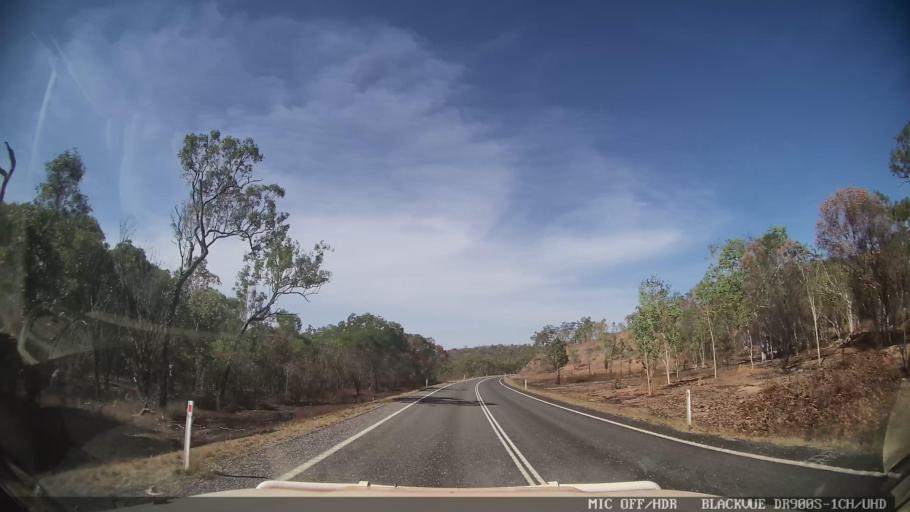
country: AU
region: Queensland
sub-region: Cook
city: Cooktown
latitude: -15.6977
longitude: 145.0293
